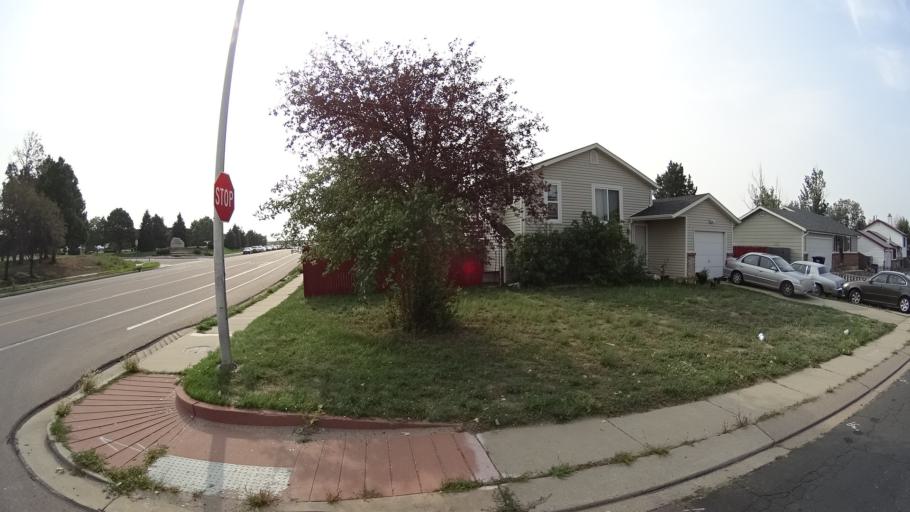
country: US
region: Colorado
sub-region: El Paso County
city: Stratmoor
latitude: 38.8039
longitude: -104.7376
